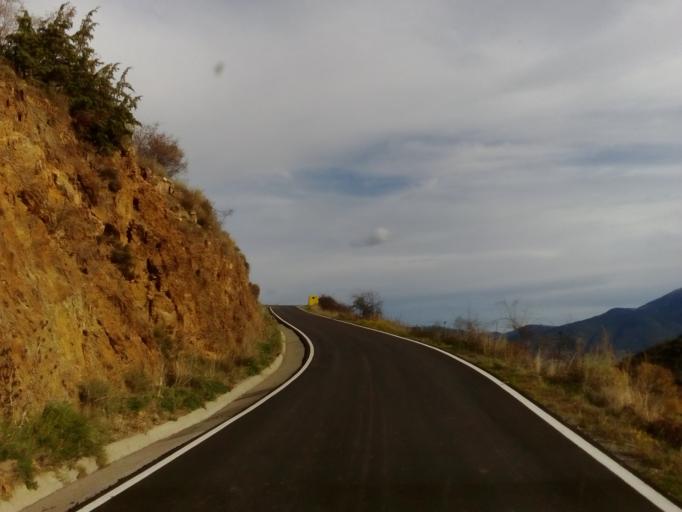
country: ES
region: Catalonia
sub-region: Provincia de Lleida
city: Eller
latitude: 42.3969
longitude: 1.7984
